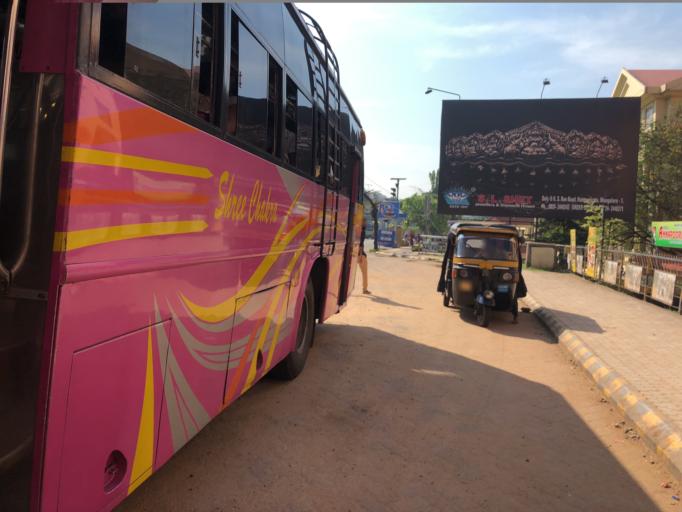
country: IN
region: Karnataka
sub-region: Dakshina Kannada
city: Mangalore
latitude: 12.8858
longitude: 74.8386
